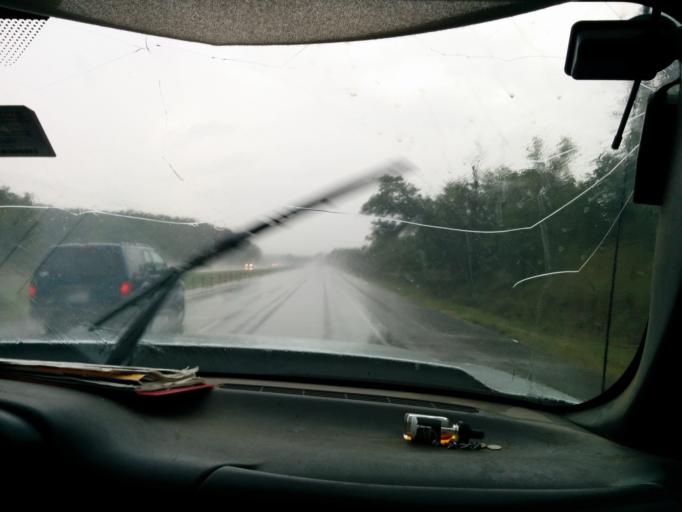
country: US
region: Oklahoma
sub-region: Okmulgee County
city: Beggs
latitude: 35.7230
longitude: -95.9989
